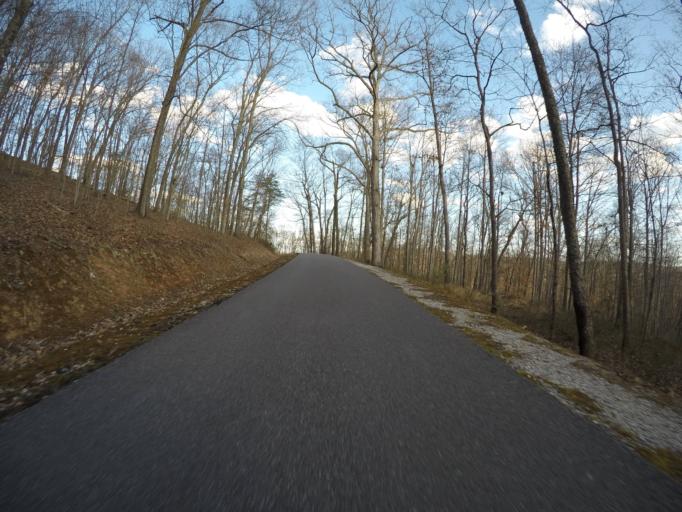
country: US
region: West Virginia
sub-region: Kanawha County
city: Charleston
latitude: 38.3889
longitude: -81.5649
